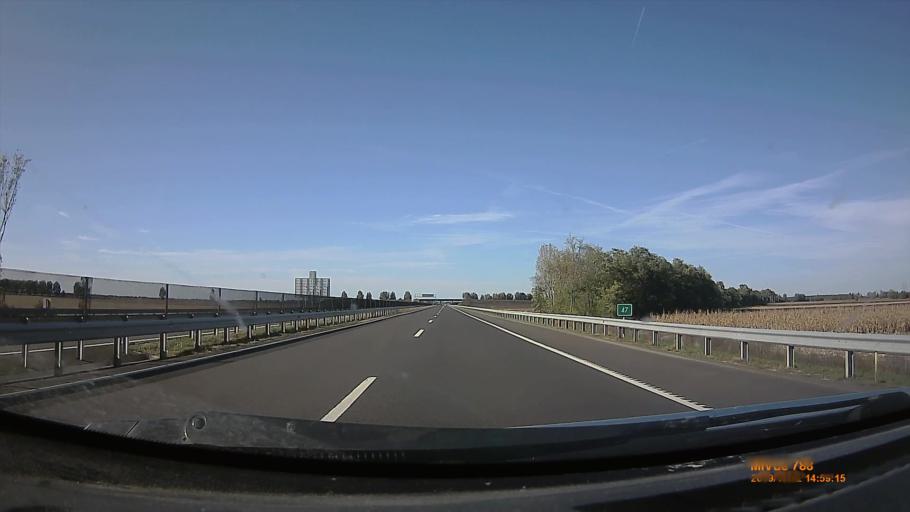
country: HU
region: Hajdu-Bihar
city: Ebes
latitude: 47.4708
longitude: 21.5607
